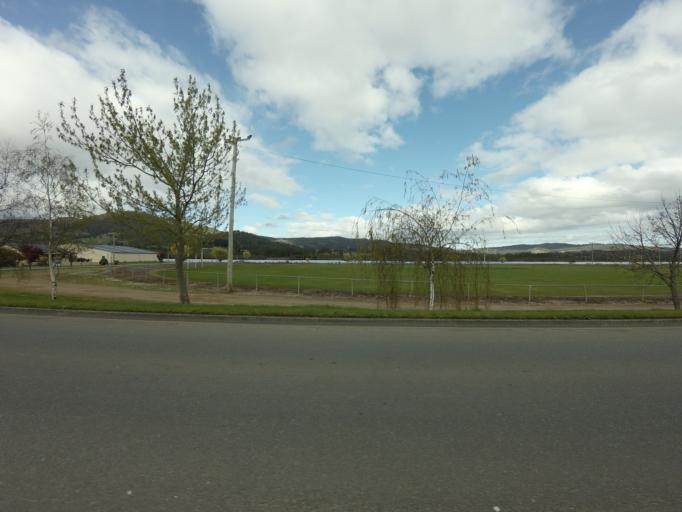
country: AU
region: Tasmania
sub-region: Huon Valley
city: Franklin
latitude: -43.0881
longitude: 147.0117
